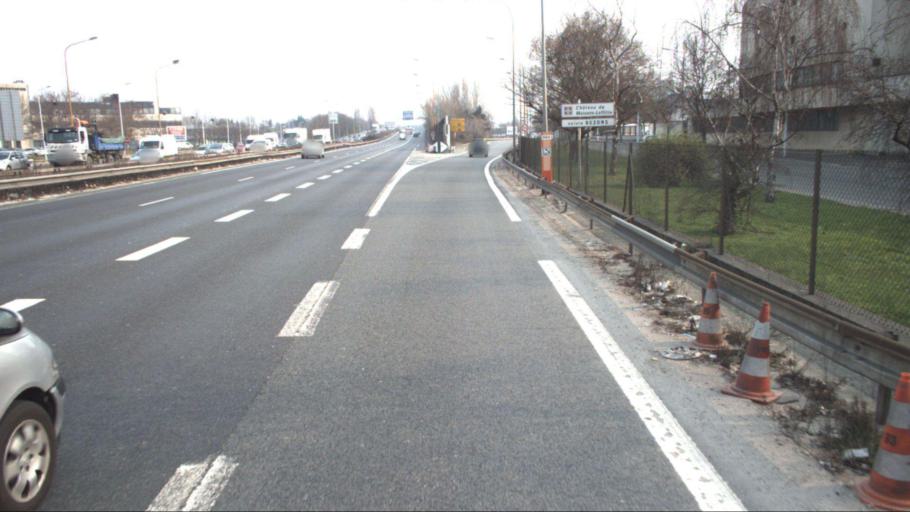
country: FR
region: Ile-de-France
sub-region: Departement du Val-d'Oise
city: Bezons
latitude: 48.9149
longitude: 2.2201
